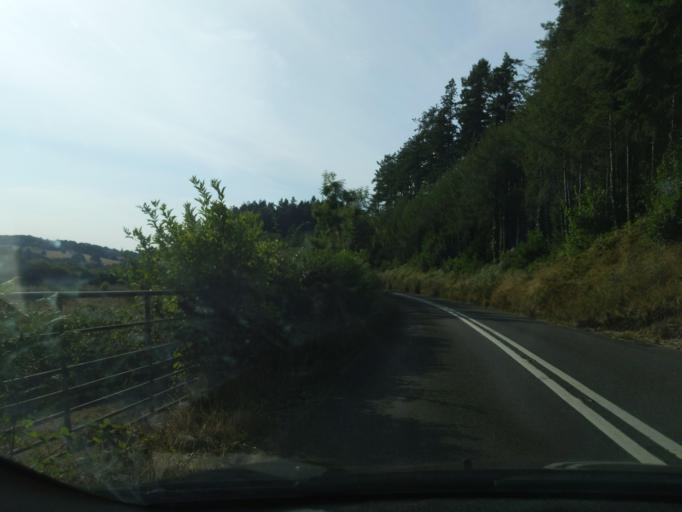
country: GB
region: England
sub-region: Devon
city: Winkleigh
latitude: 50.8869
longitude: -3.8626
